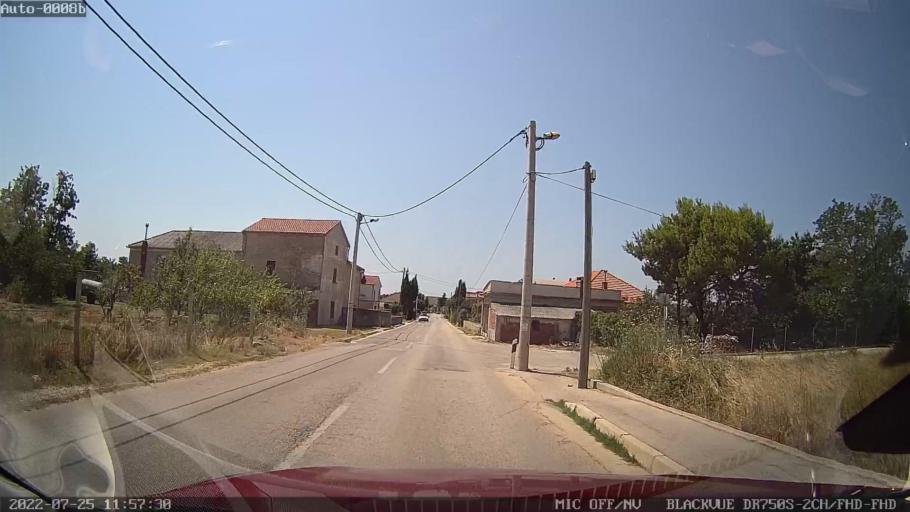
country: HR
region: Zadarska
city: Vrsi
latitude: 44.2427
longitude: 15.2139
